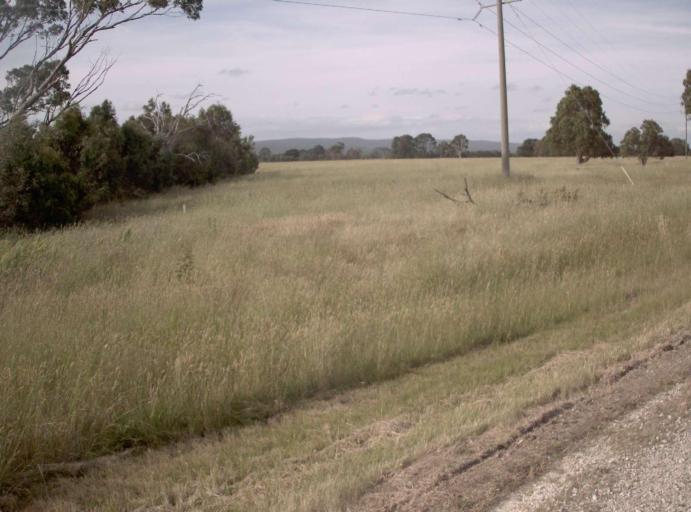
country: AU
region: Victoria
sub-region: Latrobe
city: Traralgon
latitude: -38.1099
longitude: 146.5869
